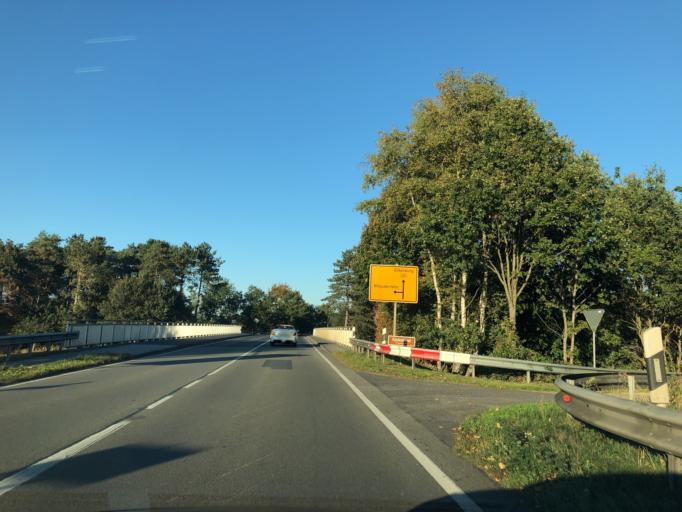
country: DE
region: Lower Saxony
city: Bockhorst
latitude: 53.0144
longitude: 7.5842
